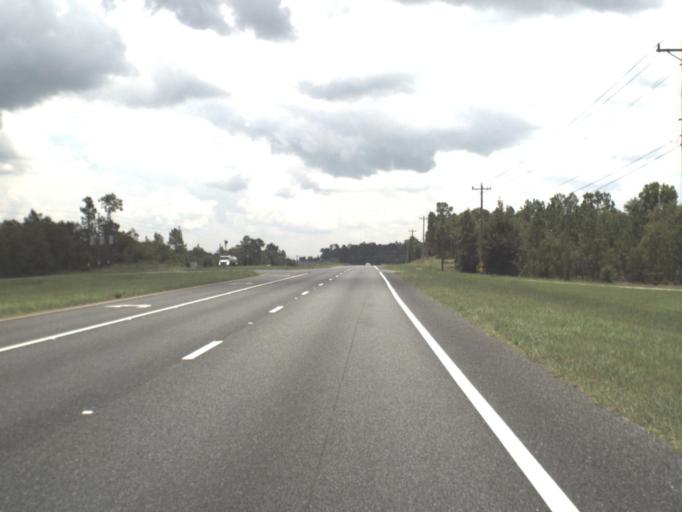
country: US
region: Florida
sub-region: Levy County
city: East Bronson
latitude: 29.4312
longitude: -82.6054
